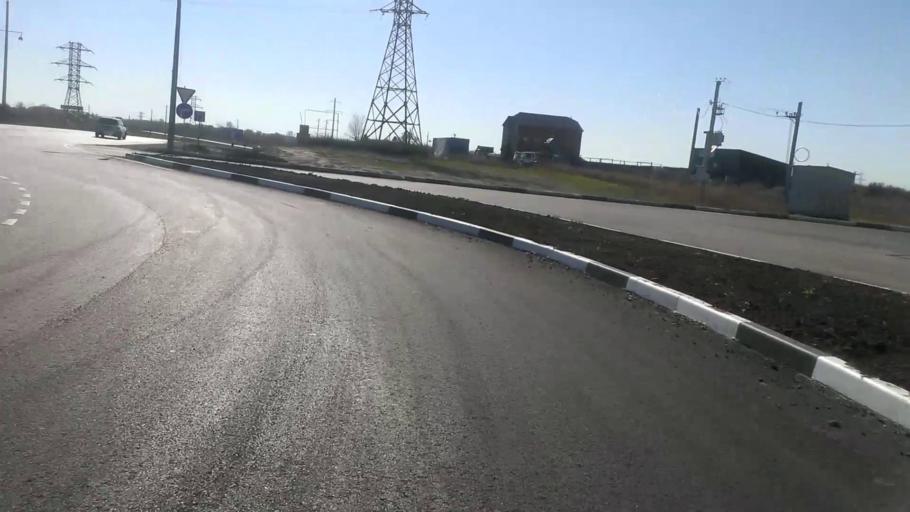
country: RU
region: Altai Krai
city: Sannikovo
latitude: 53.3367
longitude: 83.9384
